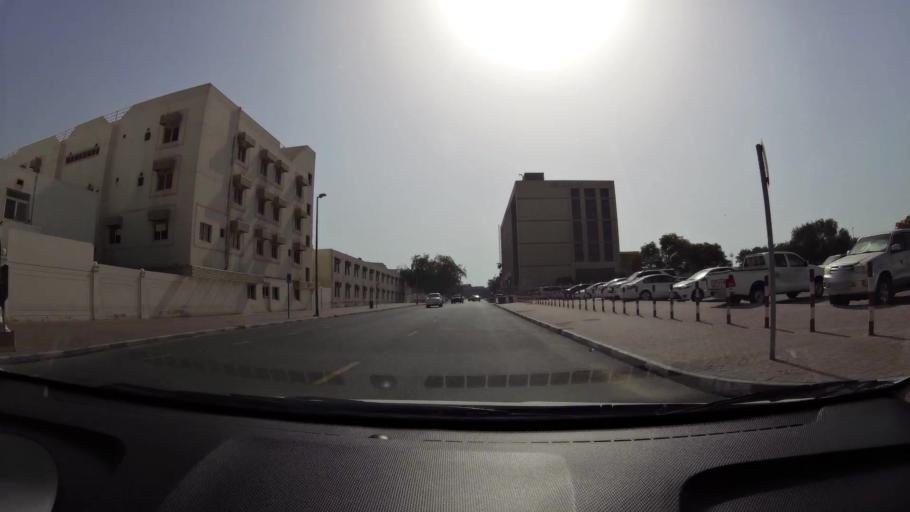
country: AE
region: Ash Shariqah
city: Sharjah
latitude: 25.2472
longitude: 55.3497
